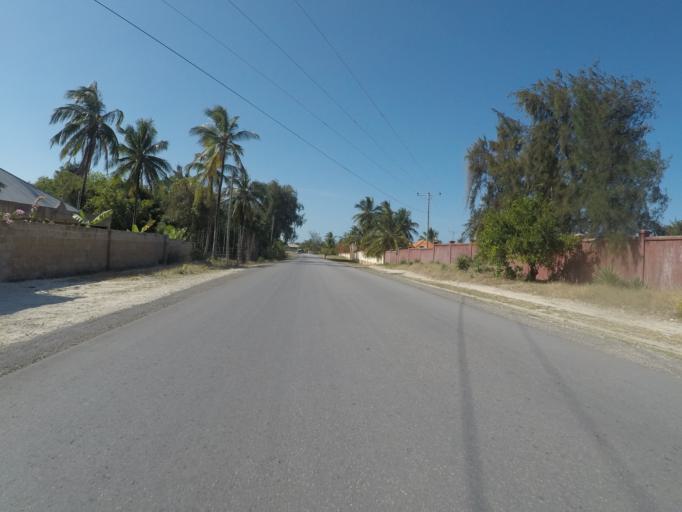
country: TZ
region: Zanzibar Central/South
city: Nganane
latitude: -6.2525
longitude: 39.5325
